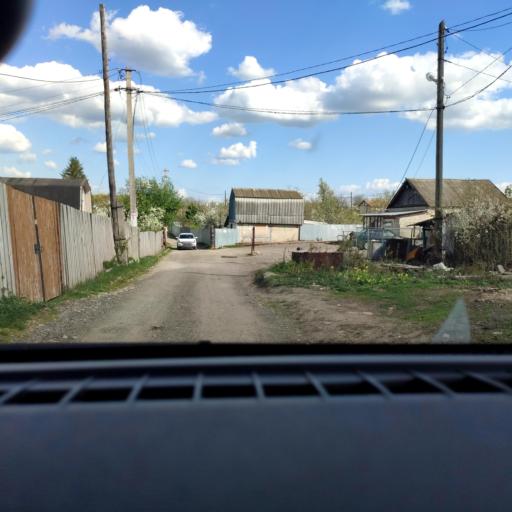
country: RU
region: Samara
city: Zhigulevsk
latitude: 53.3739
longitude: 49.4930
